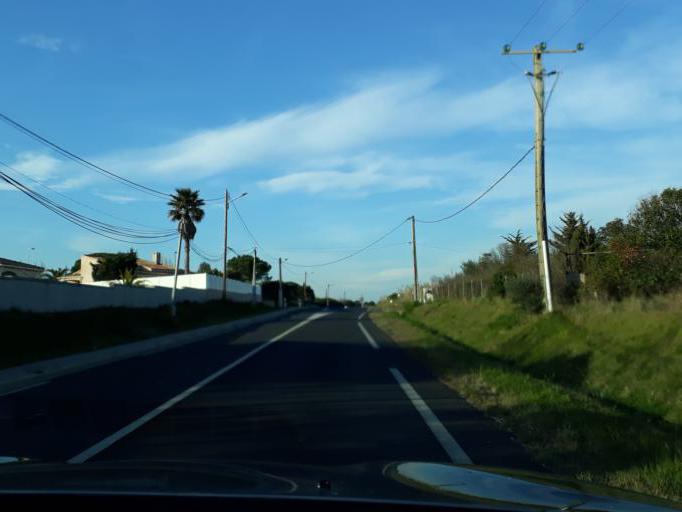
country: FR
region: Languedoc-Roussillon
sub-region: Departement de l'Herault
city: Marseillan
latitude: 43.3368
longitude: 3.5245
